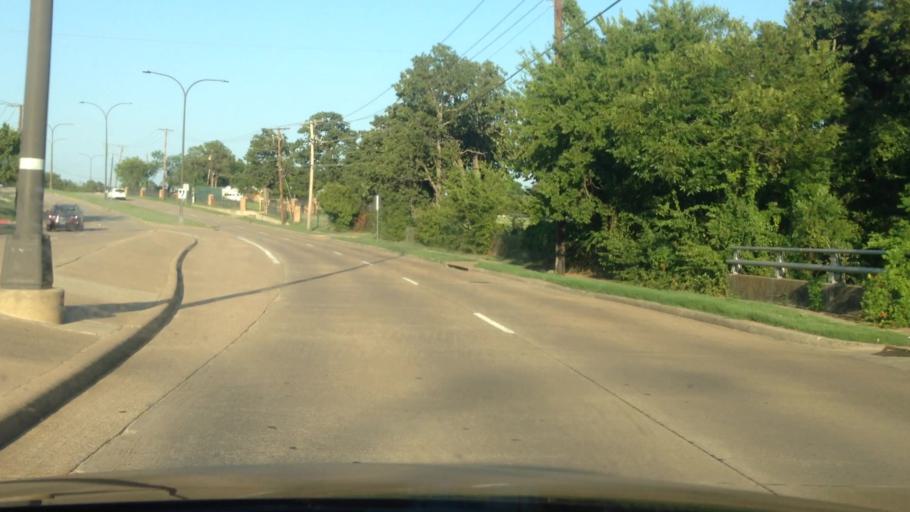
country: US
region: Texas
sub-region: Tarrant County
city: Dalworthington Gardens
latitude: 32.6815
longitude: -97.1925
